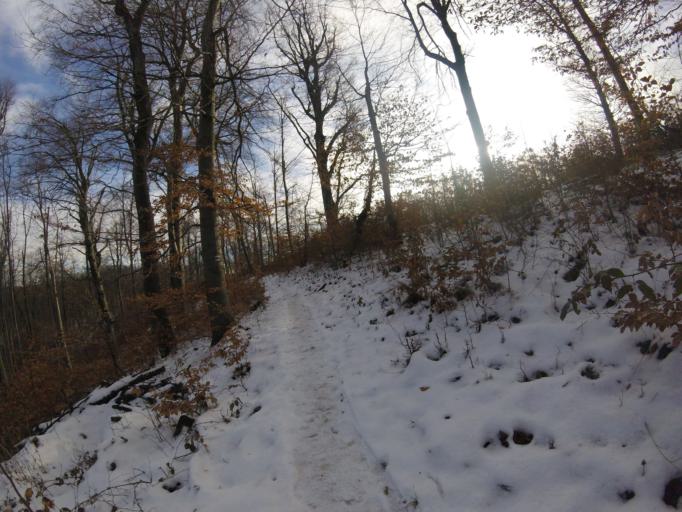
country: HU
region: Pest
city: Dunabogdany
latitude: 47.7412
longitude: 19.0208
